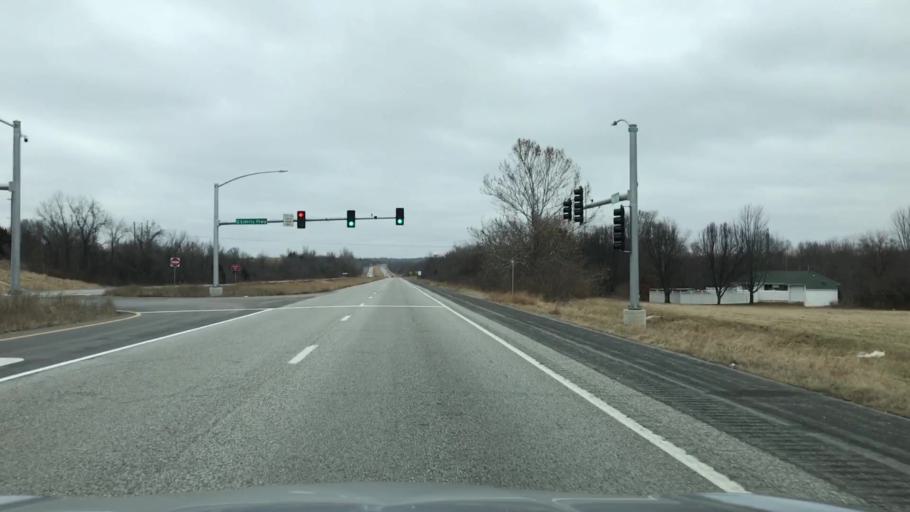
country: US
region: Missouri
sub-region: Clay County
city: Liberty
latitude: 39.2059
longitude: -94.4043
